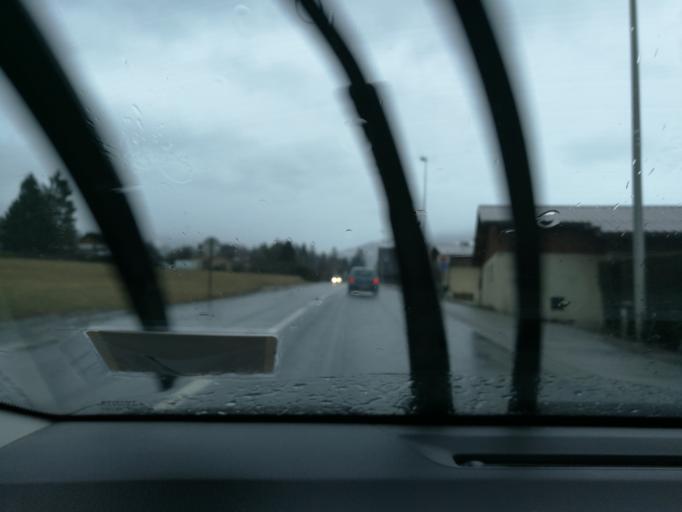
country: FR
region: Rhone-Alpes
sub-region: Departement de la Haute-Savoie
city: Domancy
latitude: 45.9306
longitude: 6.6535
